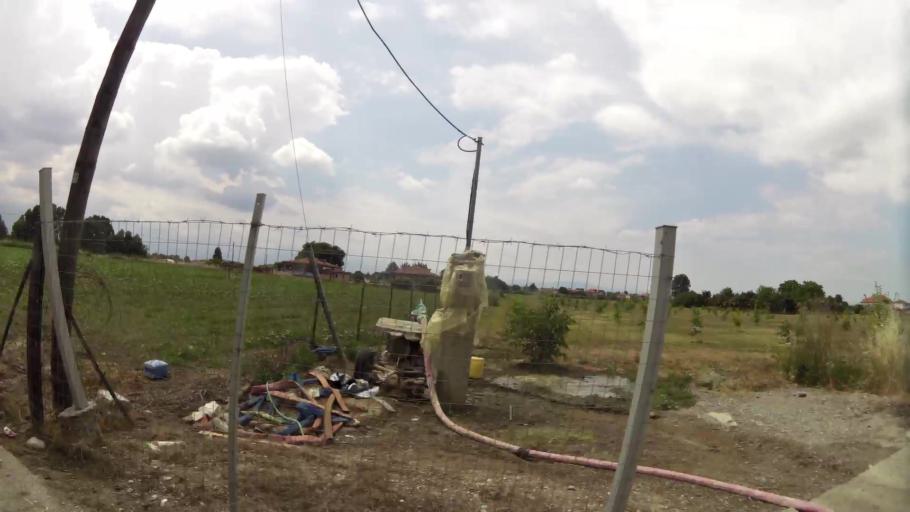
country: GR
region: Central Macedonia
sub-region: Nomos Pierias
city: Paralia
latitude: 40.2729
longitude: 22.5885
